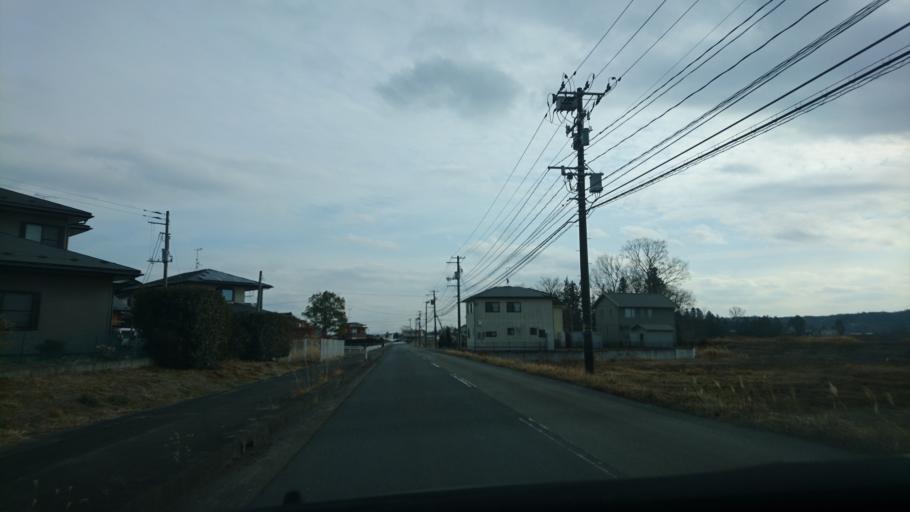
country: JP
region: Iwate
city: Ichinoseki
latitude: 38.8527
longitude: 141.1707
